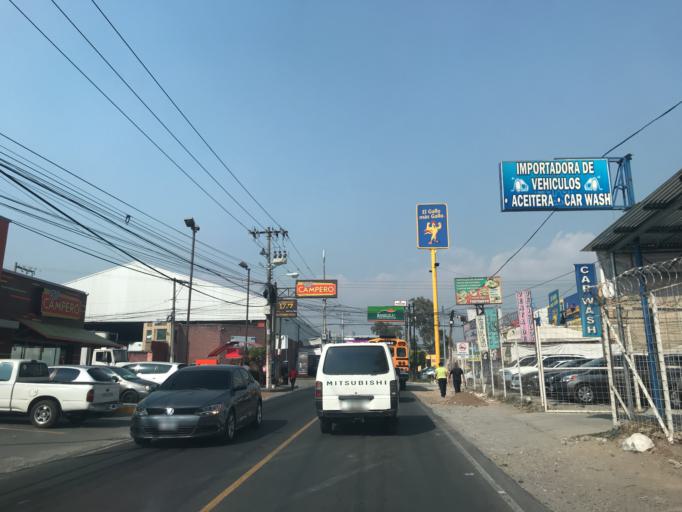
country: GT
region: Guatemala
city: Santa Catarina Pinula
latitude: 14.5497
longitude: -90.5263
